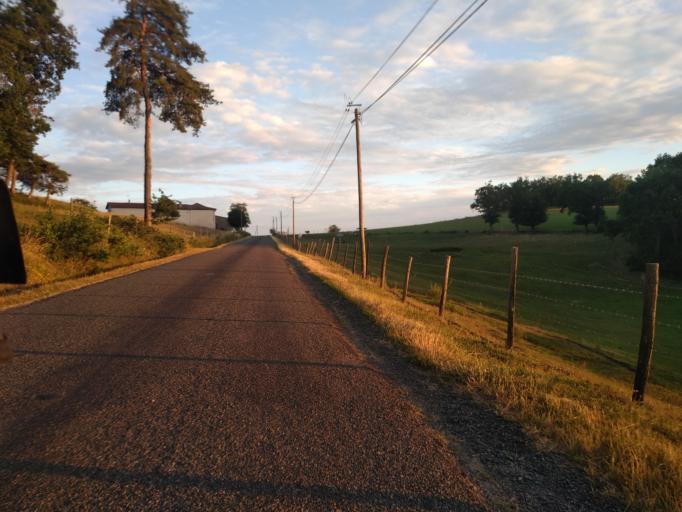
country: FR
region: Rhone-Alpes
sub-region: Departement de la Loire
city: Panissieres
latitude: 45.7499
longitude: 4.3497
